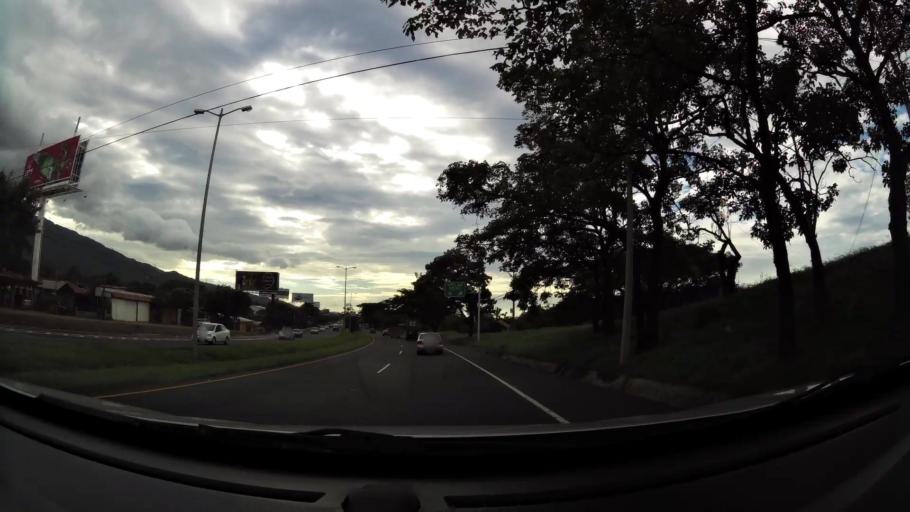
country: CR
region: San Jose
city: Santa Ana
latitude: 9.9468
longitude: -84.1854
